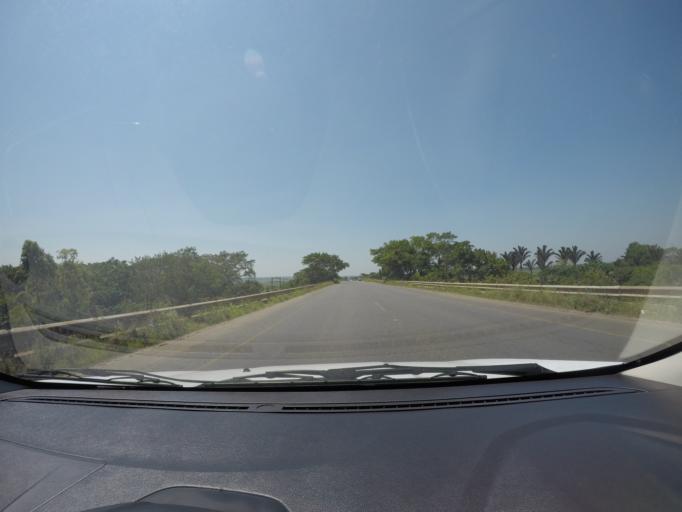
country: ZA
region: KwaZulu-Natal
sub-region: uThungulu District Municipality
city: Empangeni
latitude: -28.7993
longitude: 31.9583
